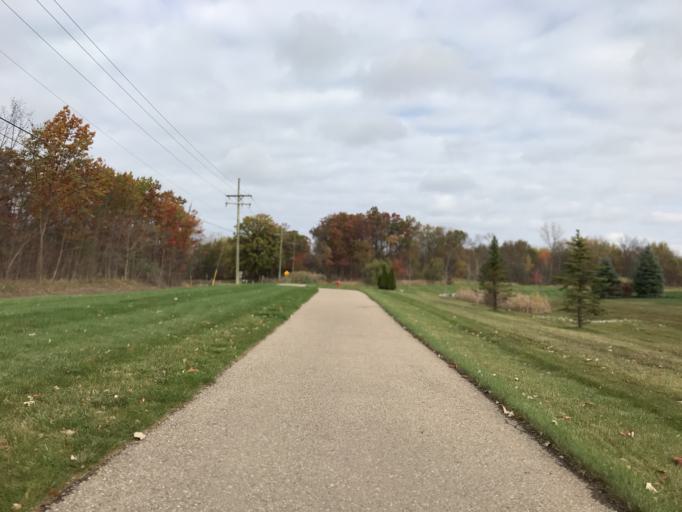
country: US
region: Michigan
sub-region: Oakland County
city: South Lyon
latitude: 42.4808
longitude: -83.6377
